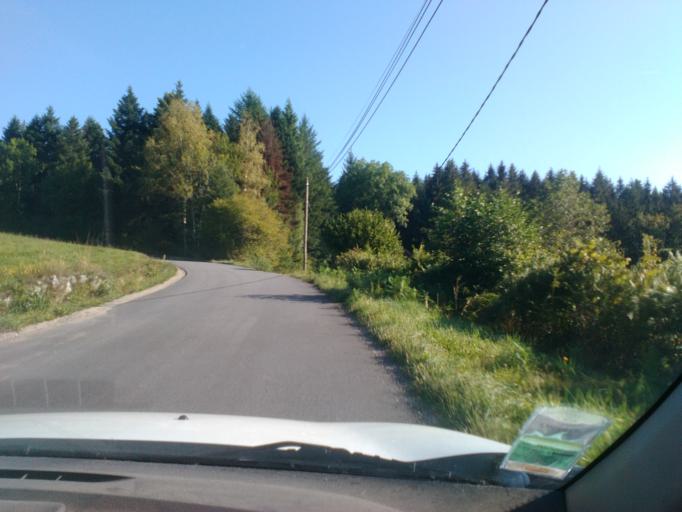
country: FR
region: Lorraine
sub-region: Departement des Vosges
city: Vagney
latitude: 48.0281
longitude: 6.7240
